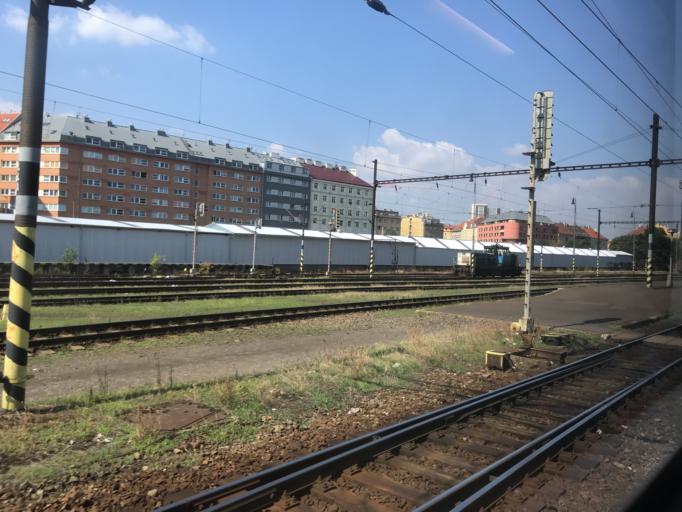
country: CZ
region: Praha
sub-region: Praha 8
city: Karlin
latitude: 50.0637
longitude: 14.4506
